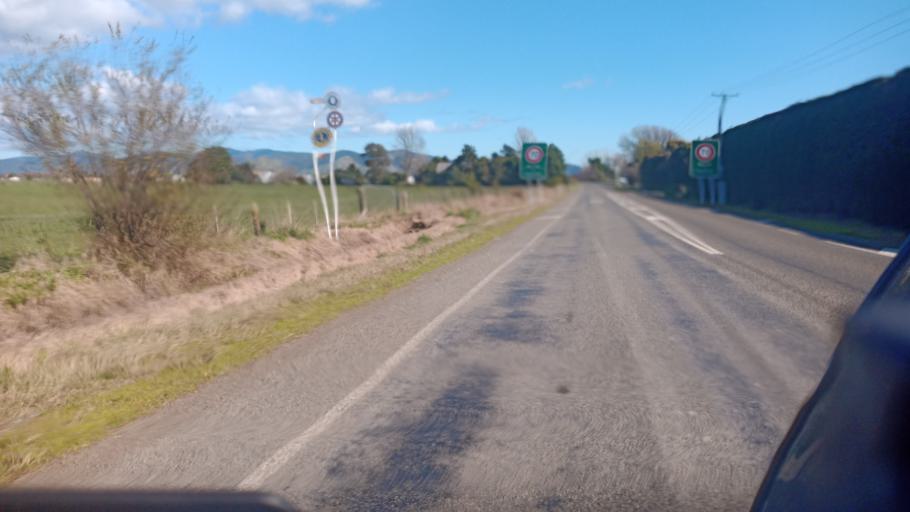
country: NZ
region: Bay of Plenty
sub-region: Opotiki District
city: Opotiki
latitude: -38.0022
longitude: 177.2958
